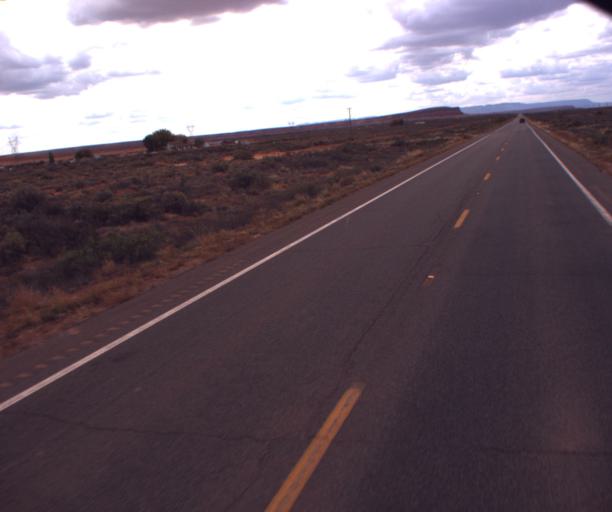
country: US
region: Arizona
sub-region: Navajo County
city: Kayenta
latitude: 36.8213
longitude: -109.8746
